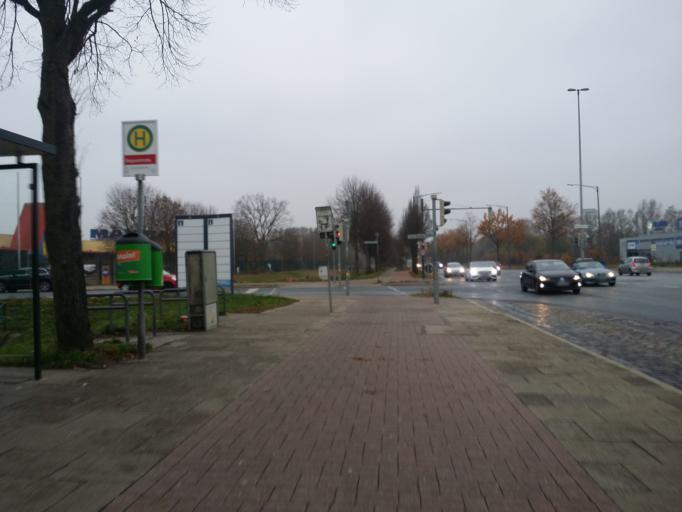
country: DE
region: Bremen
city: Bremen
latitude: 53.0461
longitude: 8.8453
